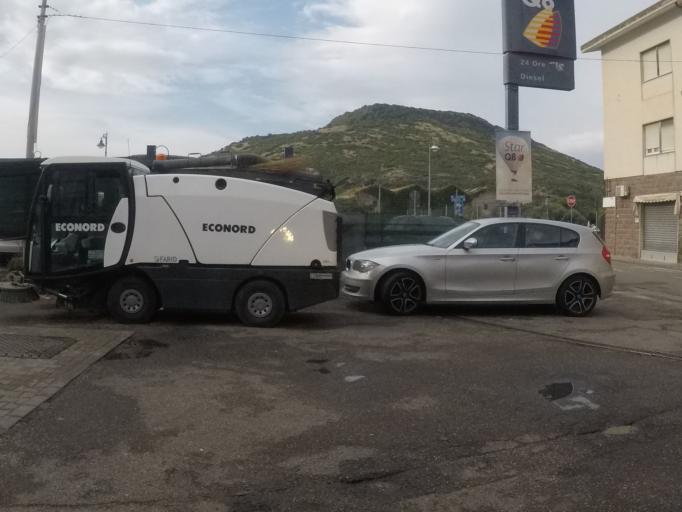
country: IT
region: Sardinia
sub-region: Provincia di Oristano
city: Bosa
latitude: 40.2957
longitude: 8.5002
